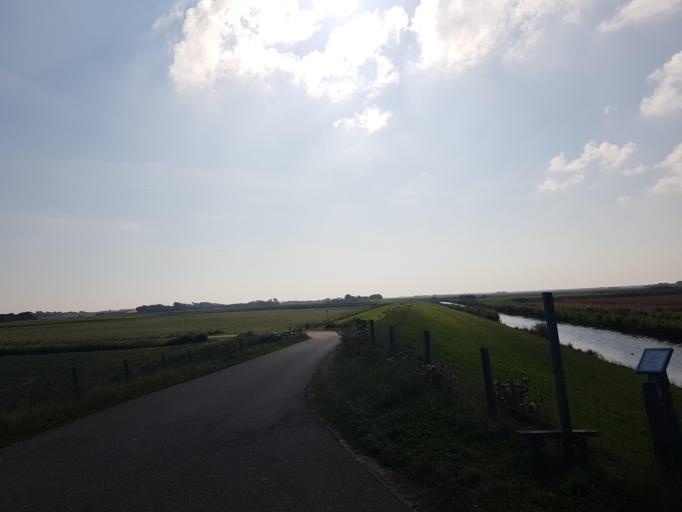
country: NL
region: North Holland
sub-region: Gemeente Texel
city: Den Burg
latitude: 53.1089
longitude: 4.8663
